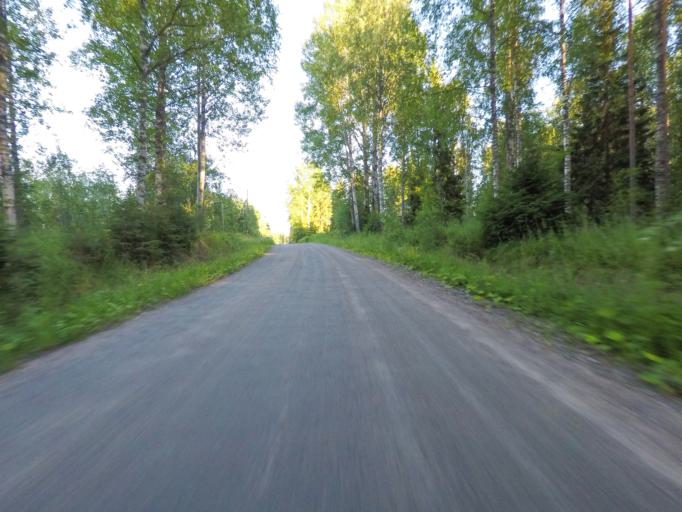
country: FI
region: Northern Savo
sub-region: Kuopio
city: Maaninka
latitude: 62.8805
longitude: 27.2935
